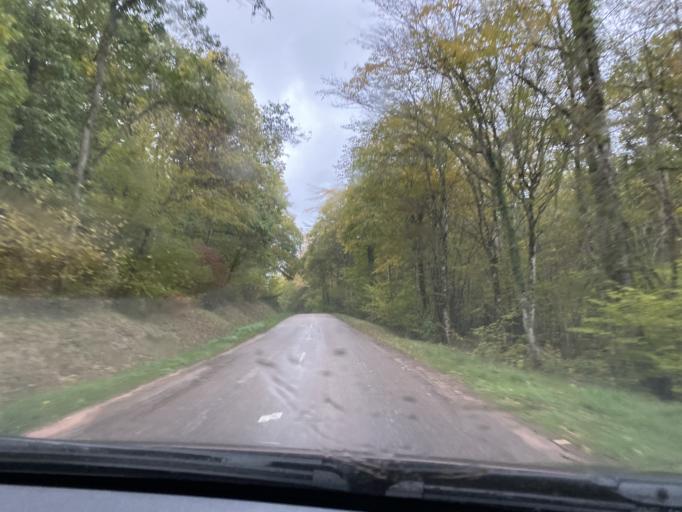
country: FR
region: Bourgogne
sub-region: Departement de la Cote-d'Or
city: Saulieu
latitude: 47.3513
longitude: 4.2400
